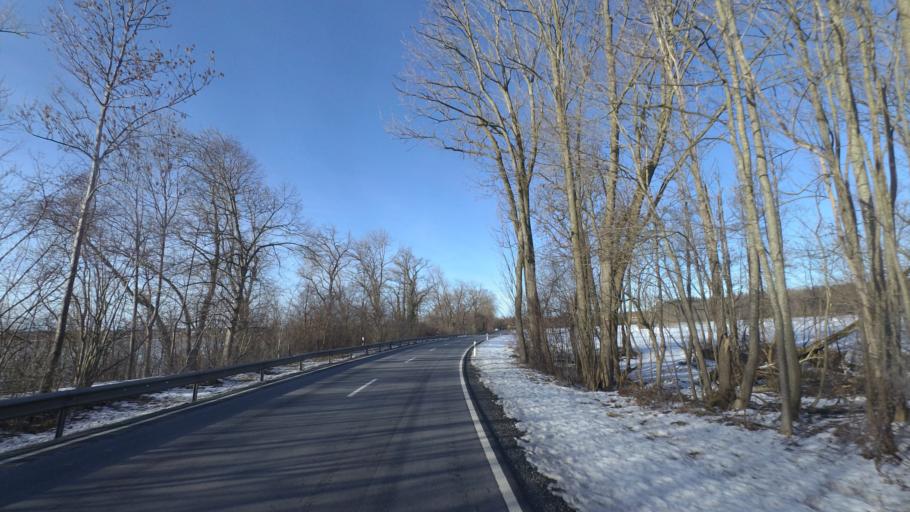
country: DE
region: Bavaria
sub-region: Upper Bavaria
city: Seeon-Seebruck
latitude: 47.9241
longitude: 12.4936
